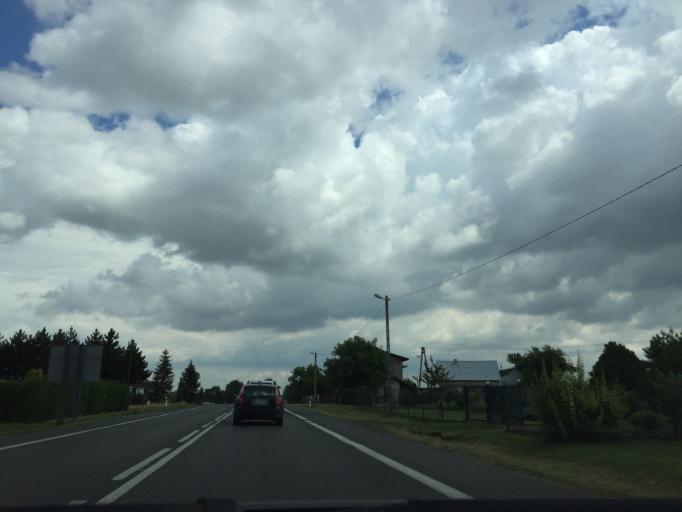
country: PL
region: Lesser Poland Voivodeship
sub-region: Powiat krakowski
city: Slomniki
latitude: 50.2239
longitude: 20.0424
